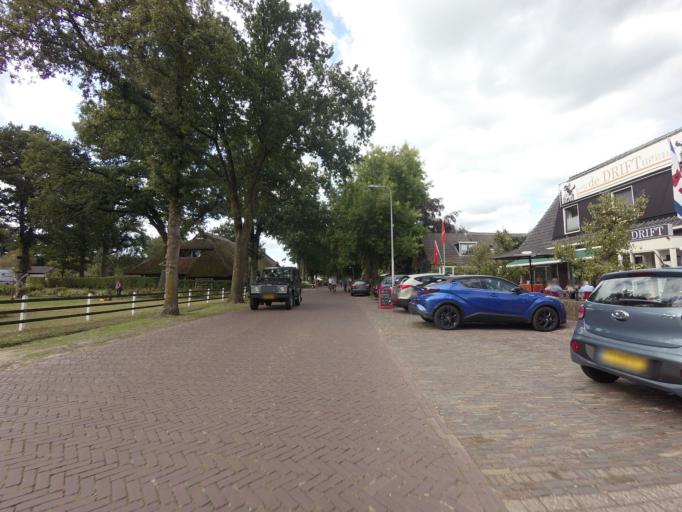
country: NL
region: Drenthe
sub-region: Gemeente Westerveld
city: Dwingeloo
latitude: 52.8309
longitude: 6.3679
